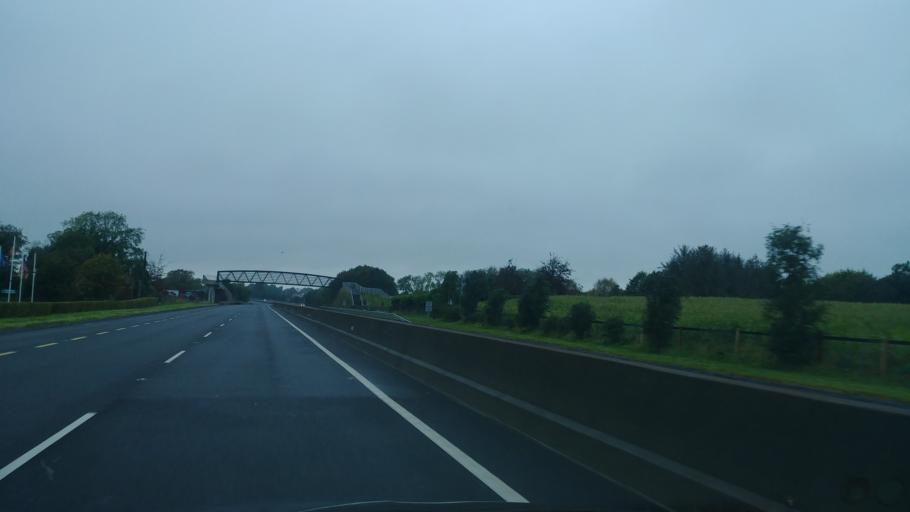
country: IE
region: Leinster
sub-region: An Iarmhi
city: Rochfortbridge
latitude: 53.5050
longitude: -7.2422
